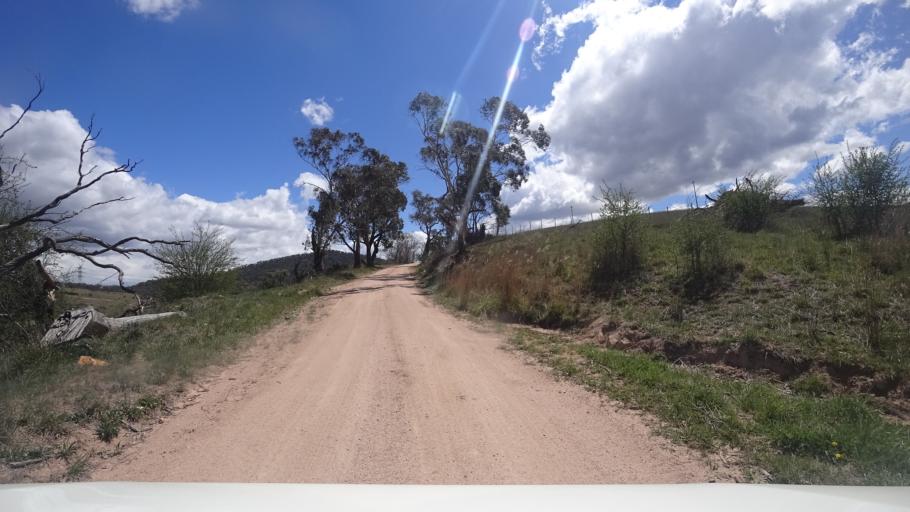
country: AU
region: New South Wales
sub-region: Oberon
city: Oberon
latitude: -33.5658
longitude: 149.9417
